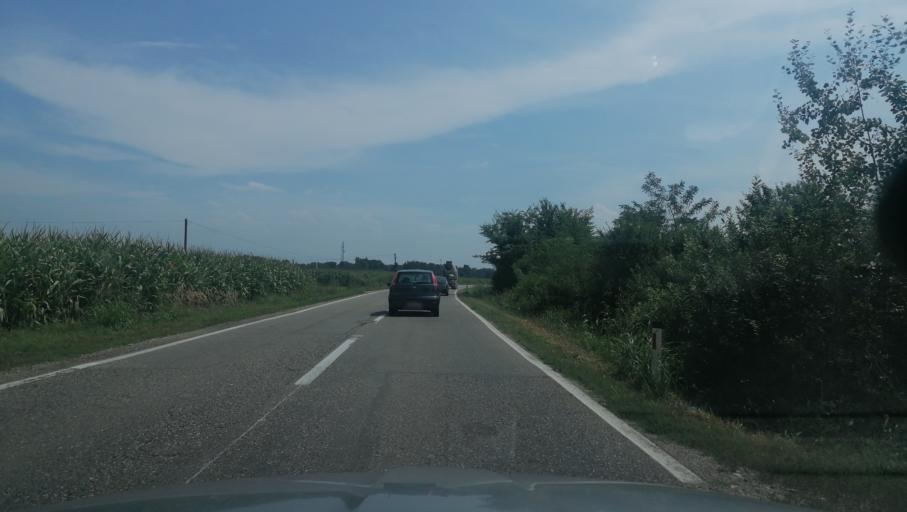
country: BA
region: Republika Srpska
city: Velika Obarska
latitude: 44.8187
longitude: 19.0527
